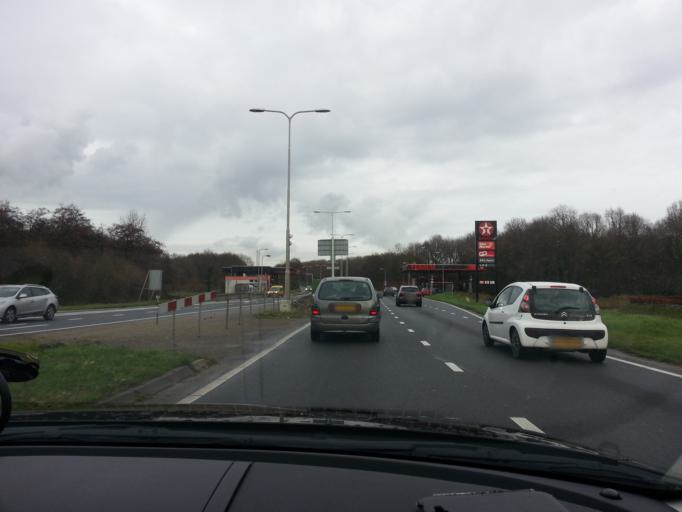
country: NL
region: South Holland
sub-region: Gemeente Spijkenisse
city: Spijkenisse
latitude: 51.8570
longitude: 4.3027
